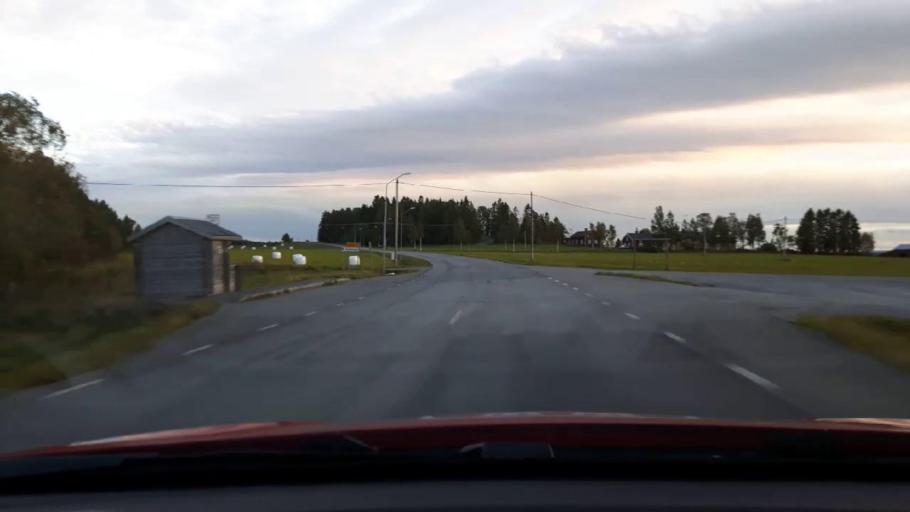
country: SE
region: Jaemtland
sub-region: OEstersunds Kommun
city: Ostersund
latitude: 63.1010
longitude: 14.4343
